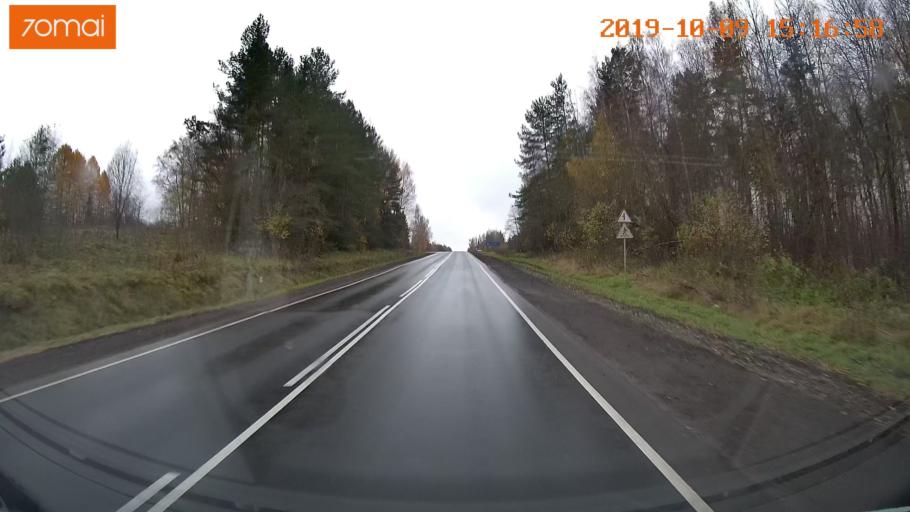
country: RU
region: Kostroma
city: Susanino
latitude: 58.1045
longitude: 41.5844
